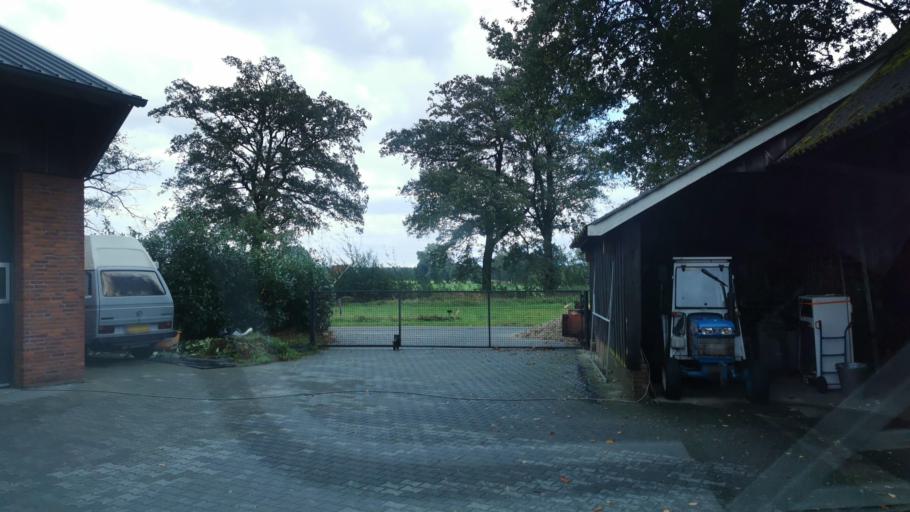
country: NL
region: Overijssel
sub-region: Gemeente Losser
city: Losser
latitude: 52.3173
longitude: 7.0151
